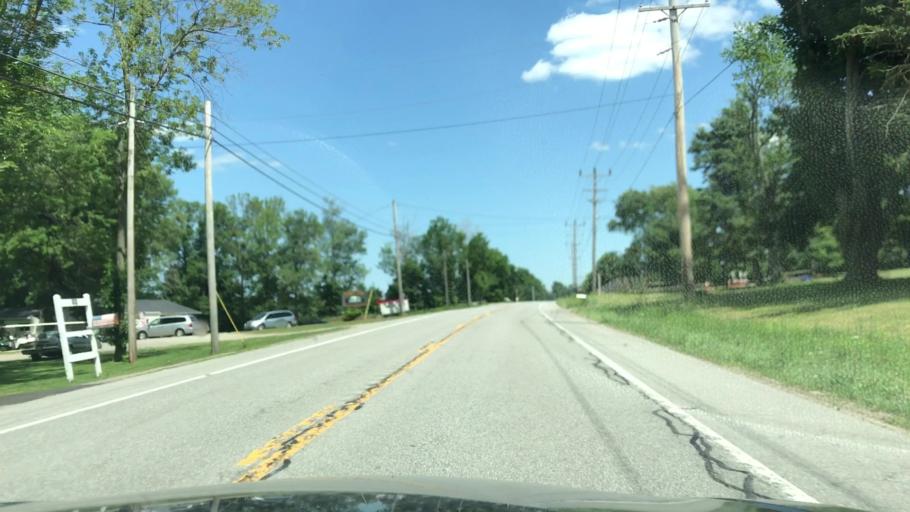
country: US
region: New York
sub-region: Wyoming County
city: Warsaw
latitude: 42.7441
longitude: -78.0675
